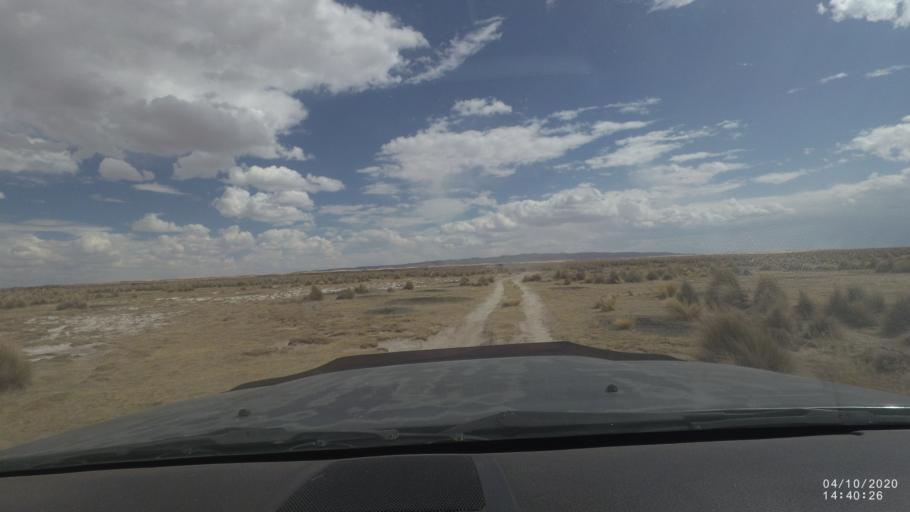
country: BO
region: Oruro
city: Poopo
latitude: -18.6794
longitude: -67.4903
